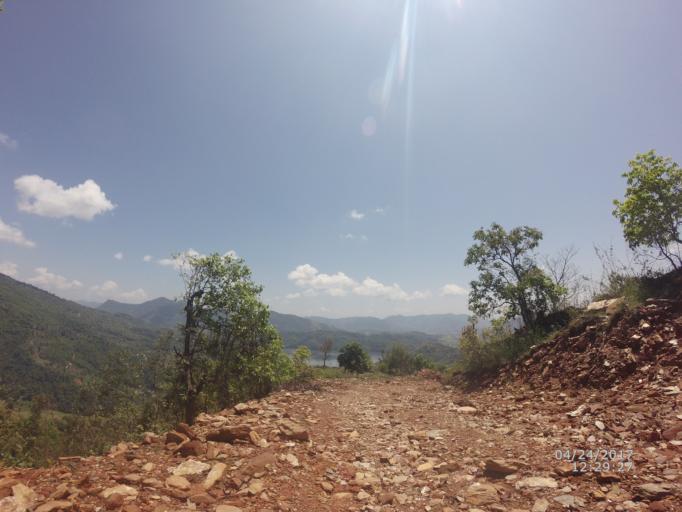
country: NP
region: Western Region
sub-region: Gandaki Zone
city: Pokhara
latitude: 28.1900
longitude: 84.0866
